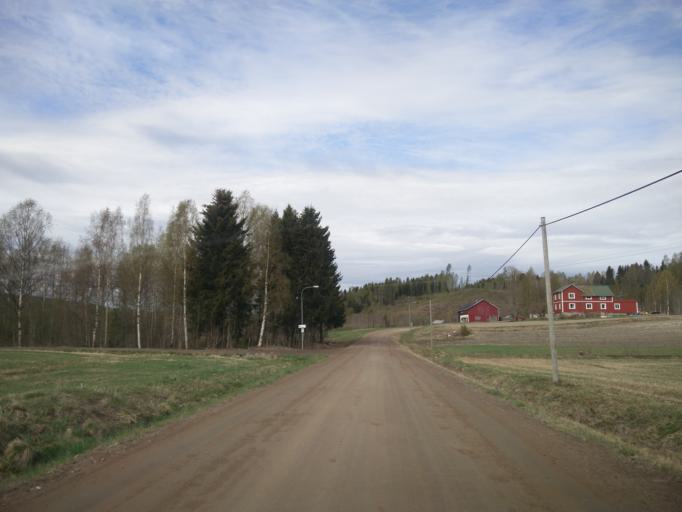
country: SE
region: Vaesternorrland
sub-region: Sundsvalls Kommun
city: Vi
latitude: 62.2728
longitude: 17.1687
